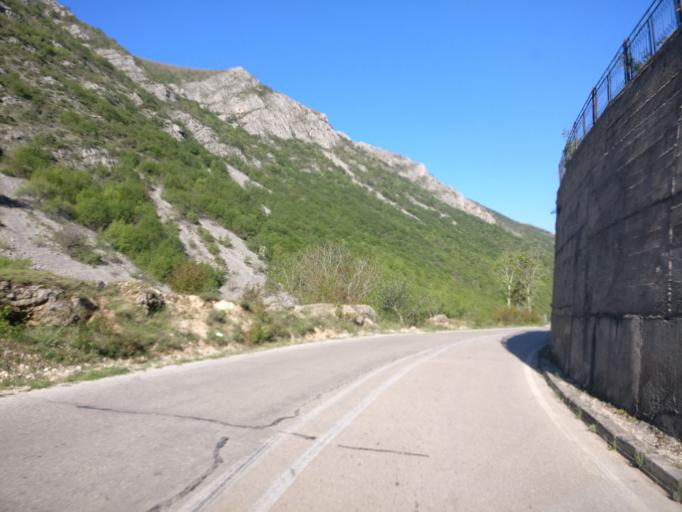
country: BA
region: Federation of Bosnia and Herzegovina
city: Stolac
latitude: 43.0786
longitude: 18.0171
